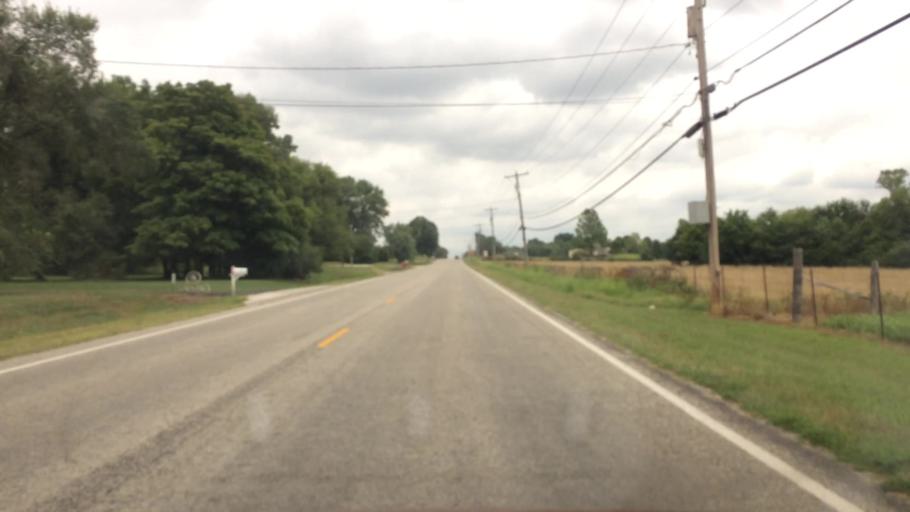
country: US
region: Missouri
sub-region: Greene County
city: Springfield
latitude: 37.2890
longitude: -93.2639
